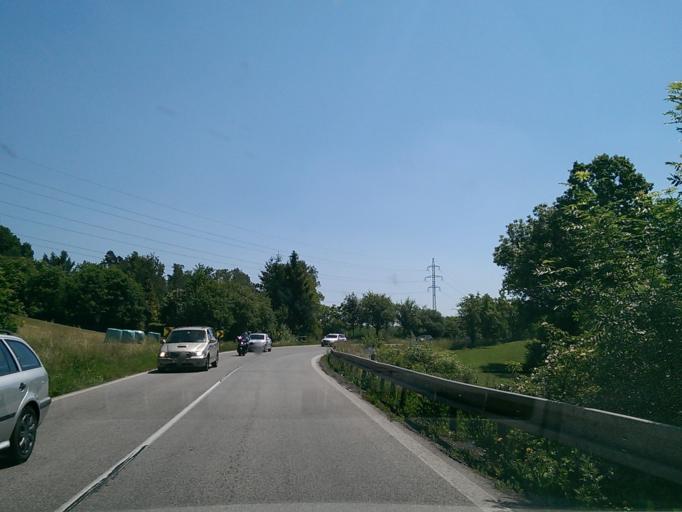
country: CZ
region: Liberecky
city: Rovensko pod Troskami
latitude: 50.5321
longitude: 15.2376
